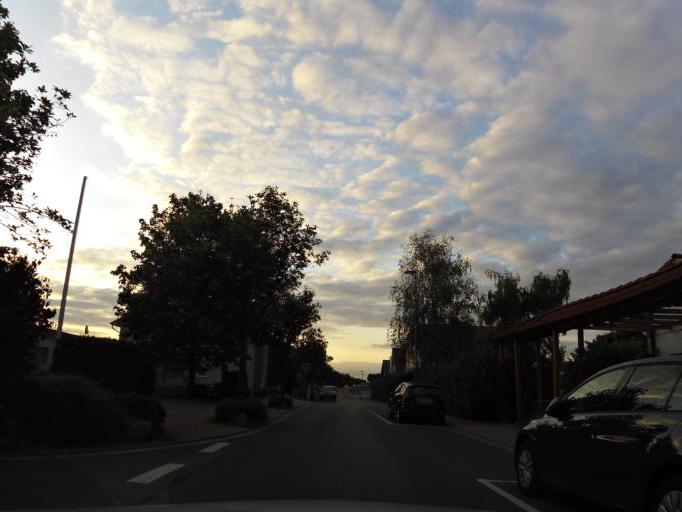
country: DE
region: Rheinland-Pfalz
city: Dexheim
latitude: 49.8448
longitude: 8.3116
